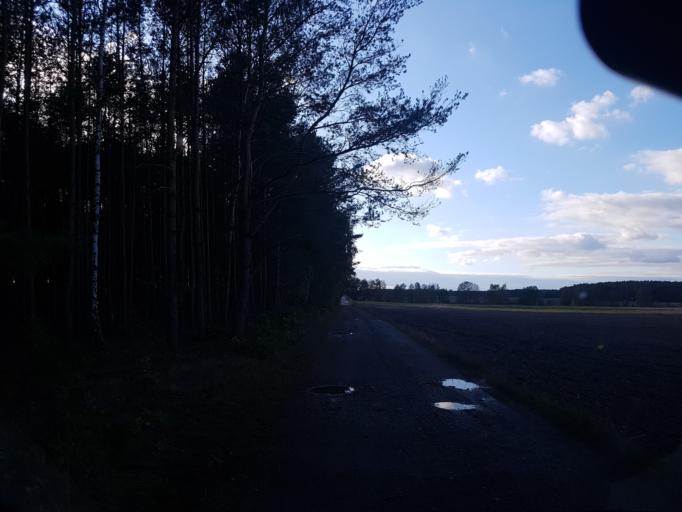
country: DE
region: Brandenburg
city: Finsterwalde
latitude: 51.5420
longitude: 13.6844
